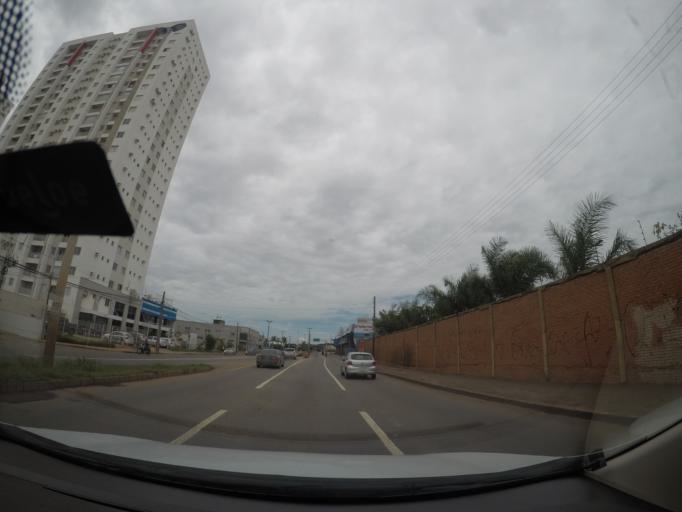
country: BR
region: Goias
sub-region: Goiania
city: Goiania
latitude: -16.6581
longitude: -49.3298
